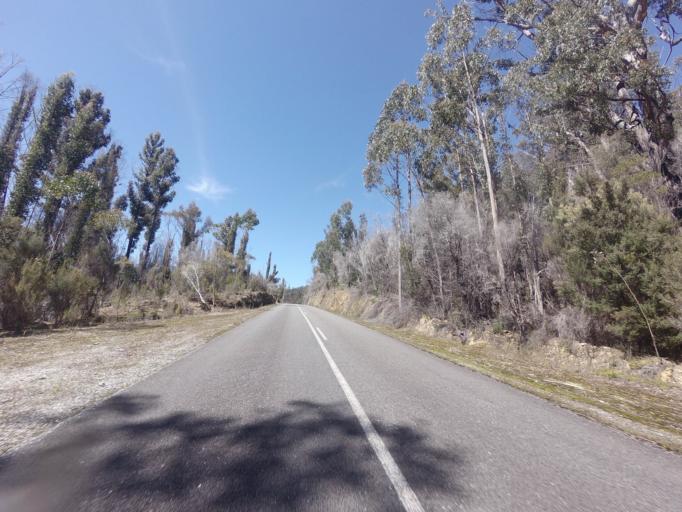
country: AU
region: Tasmania
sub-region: Huon Valley
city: Geeveston
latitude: -42.8395
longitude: 146.2582
